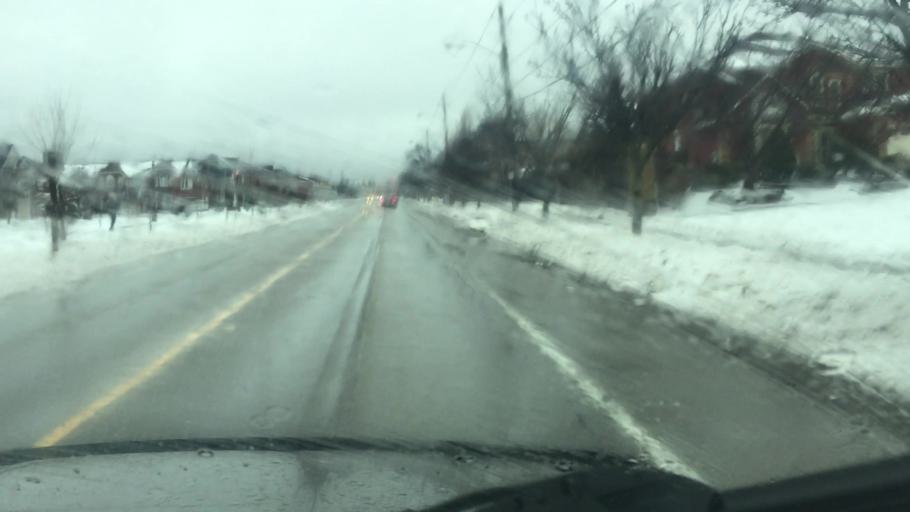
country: CA
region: Ontario
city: Ajax
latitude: 43.8629
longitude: -79.0592
